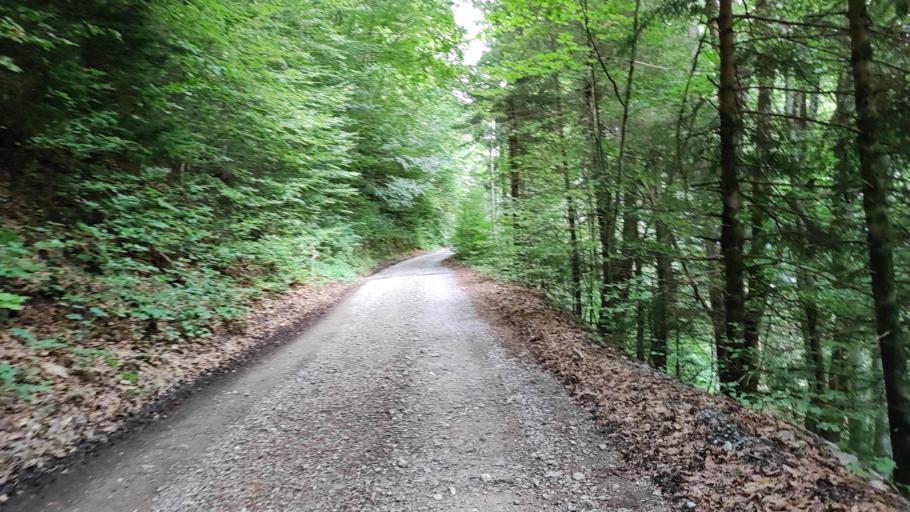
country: AT
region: Vorarlberg
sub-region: Politischer Bezirk Feldkirch
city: Feldkirch
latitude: 47.2026
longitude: 9.6088
